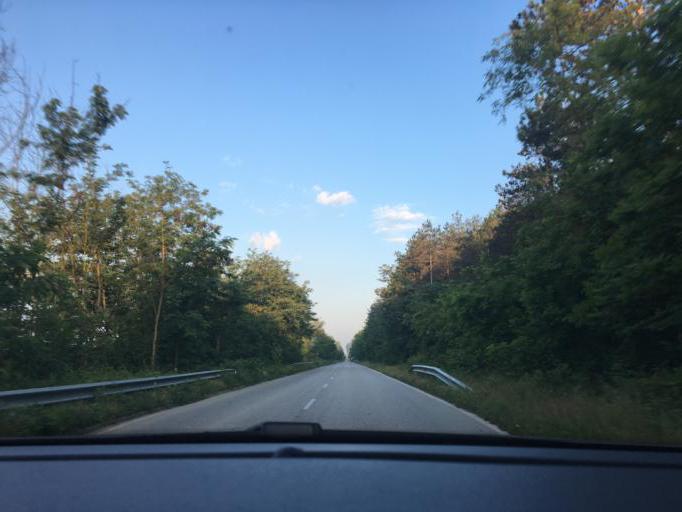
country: MK
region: Novo Selo
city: Novo Selo
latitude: 41.3963
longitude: 23.0105
